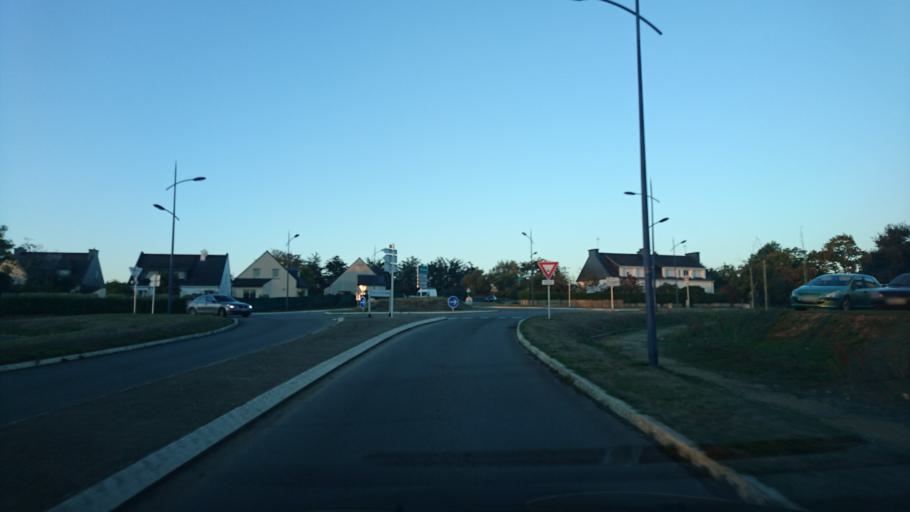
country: FR
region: Brittany
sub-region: Departement du Morbihan
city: Pluneret
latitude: 47.6657
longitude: -2.9672
